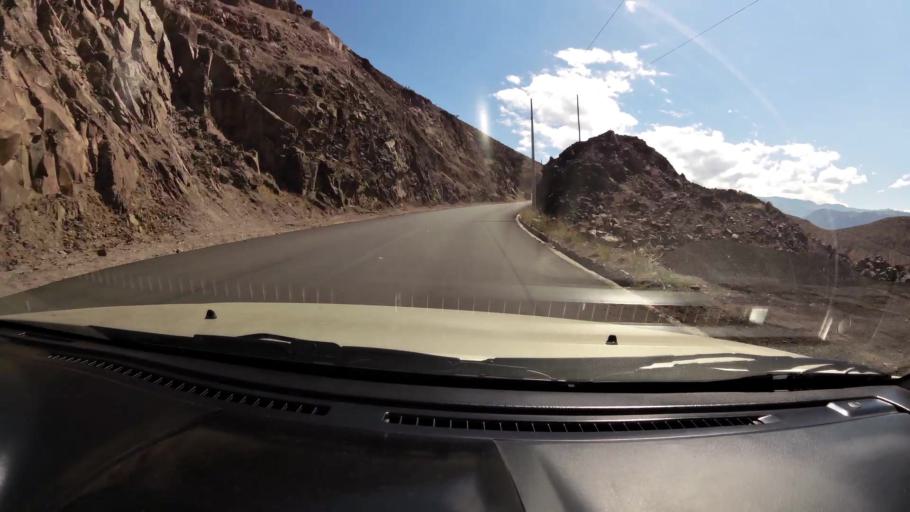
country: EC
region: El Oro
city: Zaruma
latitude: -3.3429
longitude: -79.3873
